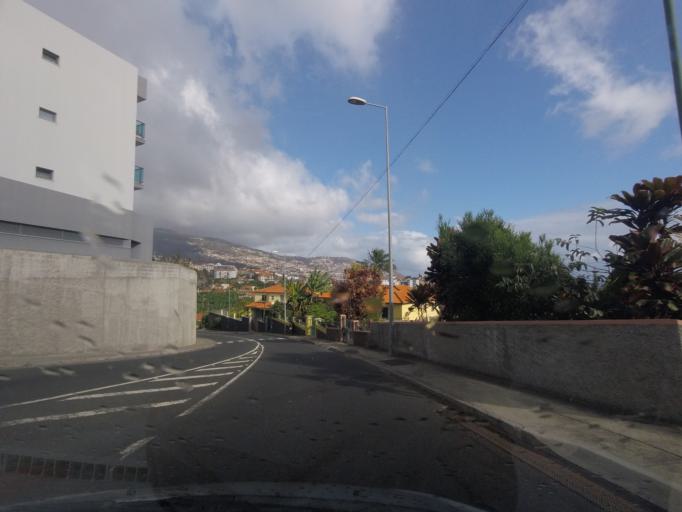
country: PT
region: Madeira
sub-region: Funchal
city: Nossa Senhora do Monte
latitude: 32.6544
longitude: -16.9307
